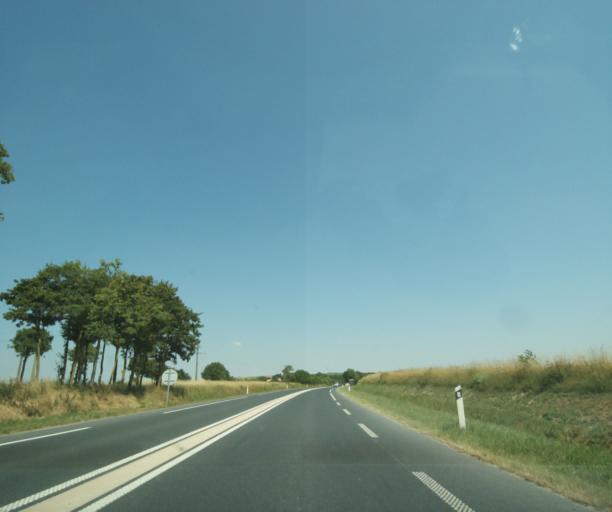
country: FR
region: Champagne-Ardenne
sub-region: Departement de la Marne
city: Fagnieres
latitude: 49.0601
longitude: 4.2975
